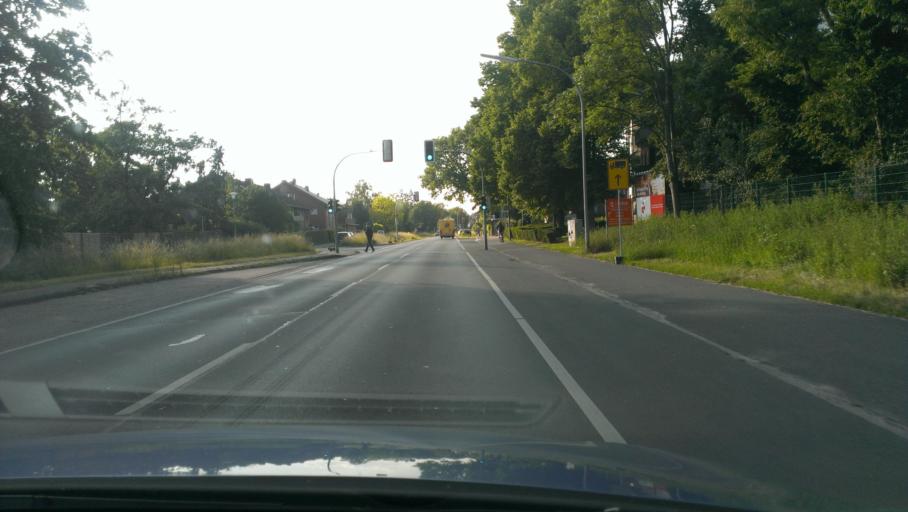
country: DE
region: North Rhine-Westphalia
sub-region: Regierungsbezirk Munster
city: Muenster
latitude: 51.9184
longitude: 7.6786
